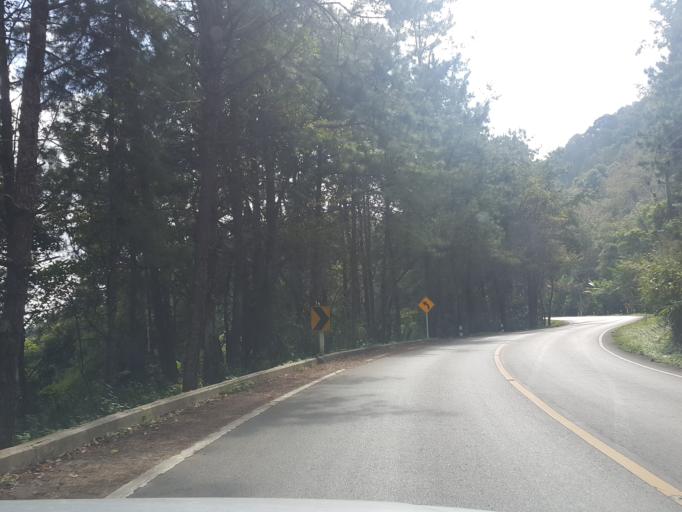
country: TH
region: Chiang Mai
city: Mae Chaem
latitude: 18.5140
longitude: 98.5143
